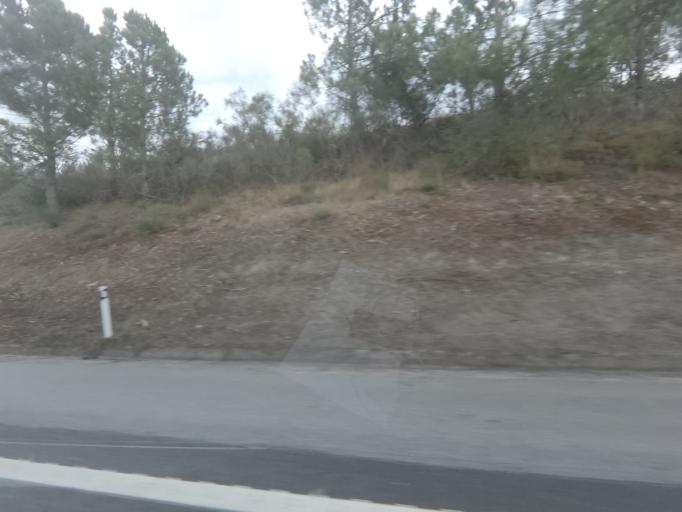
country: PT
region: Viseu
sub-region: Lamego
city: Lamego
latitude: 41.0544
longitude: -7.8402
